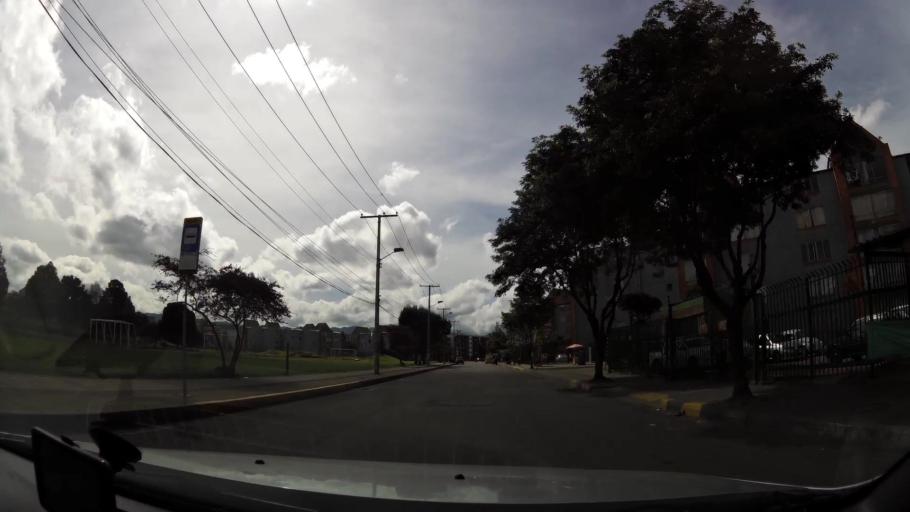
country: CO
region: Bogota D.C.
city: Bogota
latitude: 4.6446
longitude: -74.1426
